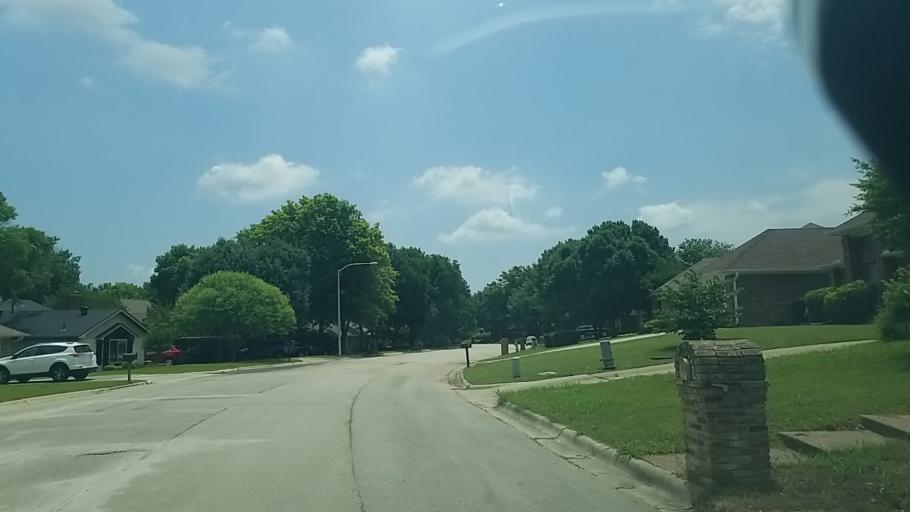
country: US
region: Texas
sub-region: Denton County
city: Corinth
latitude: 33.1645
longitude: -97.0883
